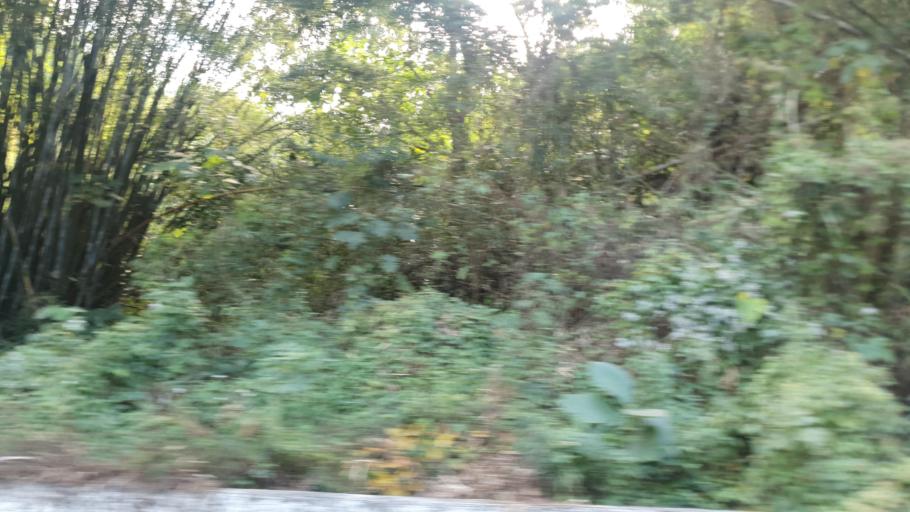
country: TW
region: Taiwan
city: Yujing
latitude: 23.0261
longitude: 120.3948
